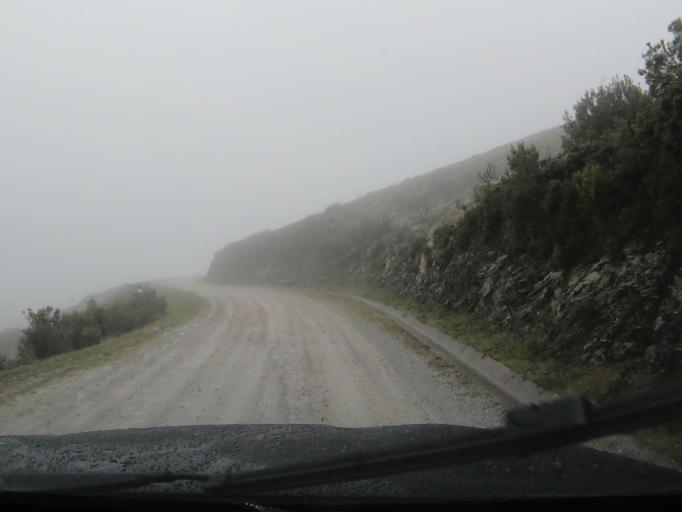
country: PT
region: Vila Real
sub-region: Vila Real
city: Vila Real
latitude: 41.3222
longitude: -7.8616
